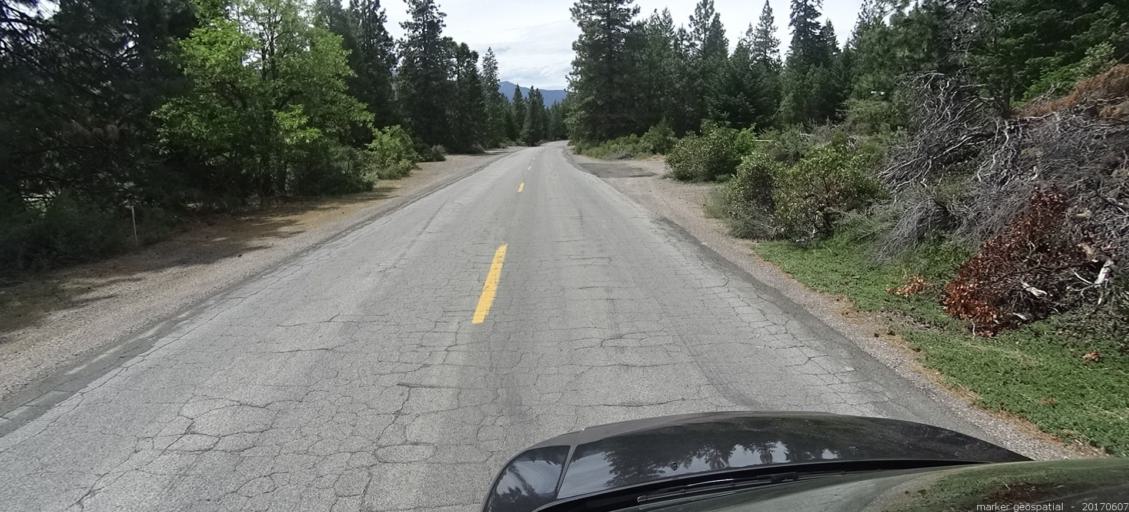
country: US
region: California
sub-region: Siskiyou County
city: Mount Shasta
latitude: 41.3413
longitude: -122.3464
